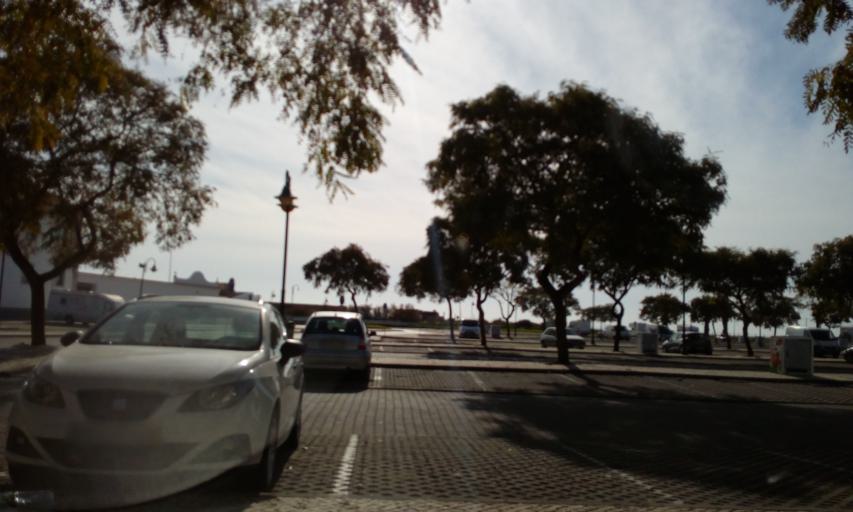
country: PT
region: Faro
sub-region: Faro
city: Faro
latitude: 37.0127
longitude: -7.9315
